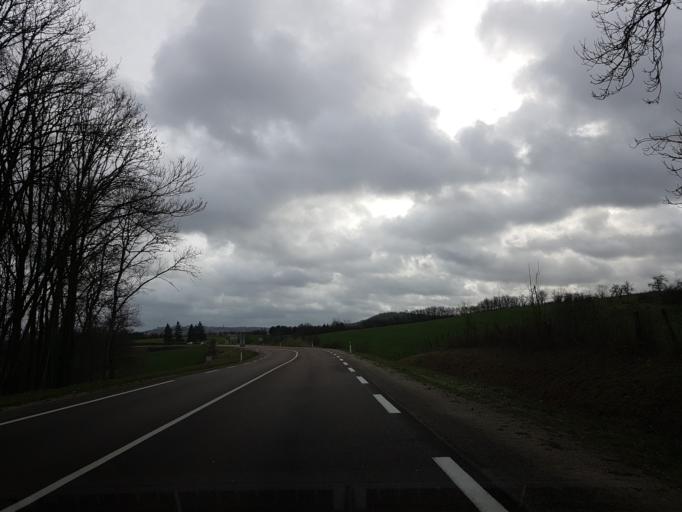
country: FR
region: Champagne-Ardenne
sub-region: Departement de la Haute-Marne
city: Rolampont
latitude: 47.9106
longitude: 5.2917
